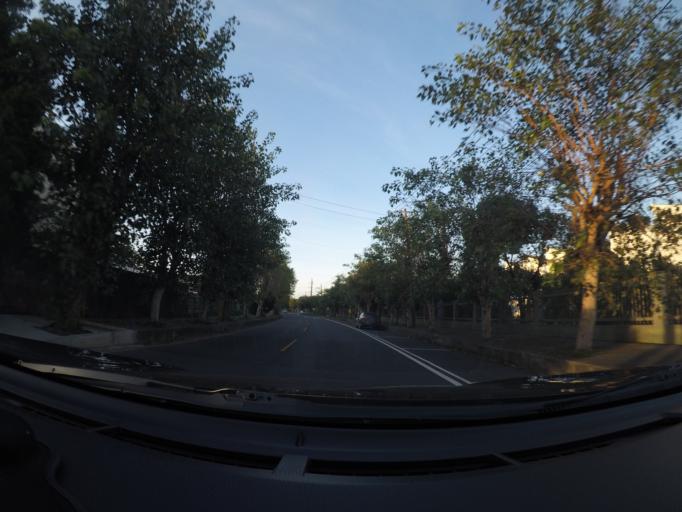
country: TW
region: Taiwan
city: Taoyuan City
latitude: 24.9906
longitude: 121.2464
